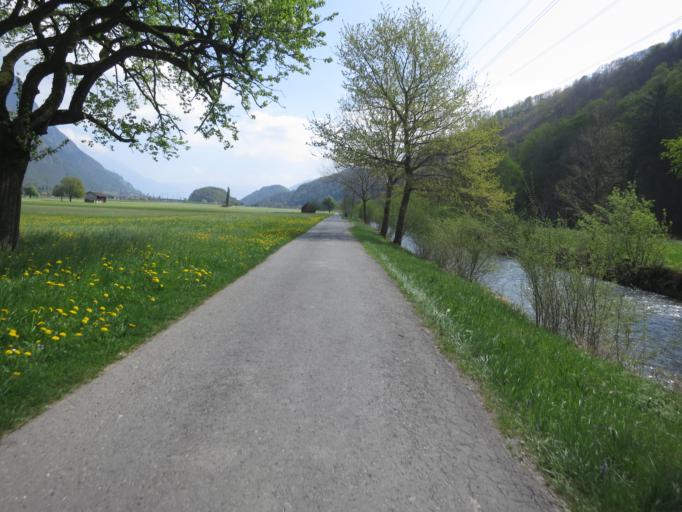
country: CH
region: Saint Gallen
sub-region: Wahlkreis Sarganserland
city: Flums
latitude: 47.0738
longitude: 9.3724
